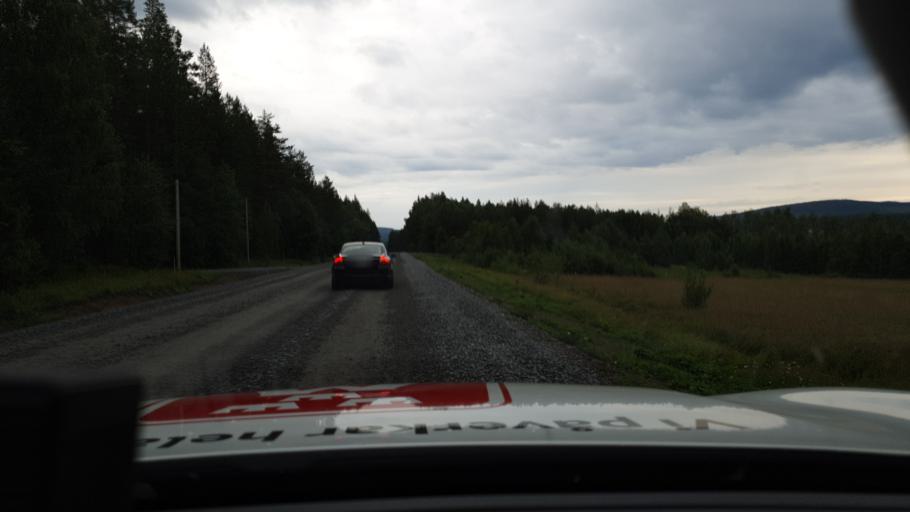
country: SE
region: Norrbotten
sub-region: Bodens Kommun
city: Boden
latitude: 65.8732
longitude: 21.4111
